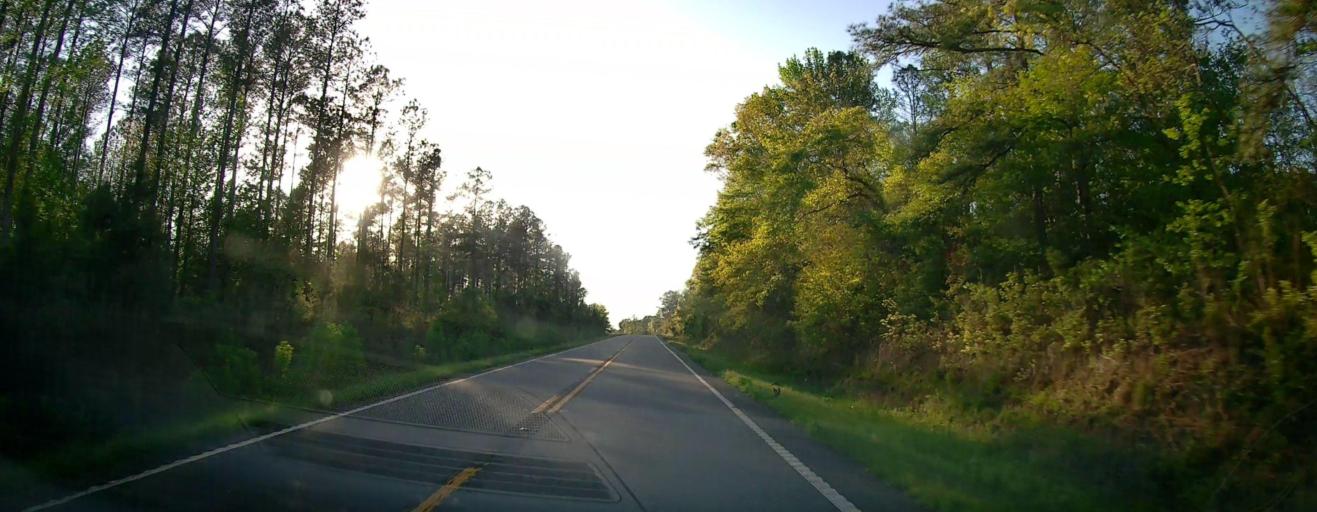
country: US
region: Georgia
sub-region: Schley County
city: Ellaville
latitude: 32.3276
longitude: -84.3304
